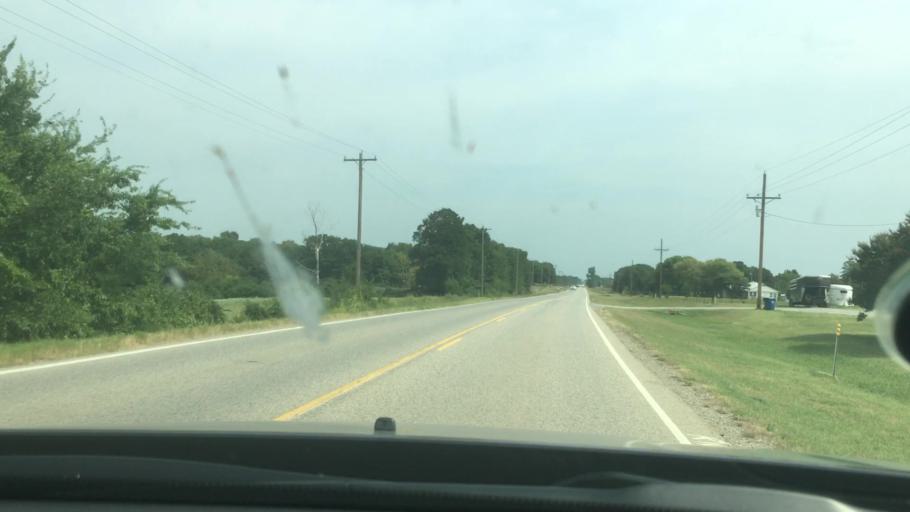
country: US
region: Oklahoma
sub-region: Bryan County
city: Durant
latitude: 34.2025
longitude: -96.4250
